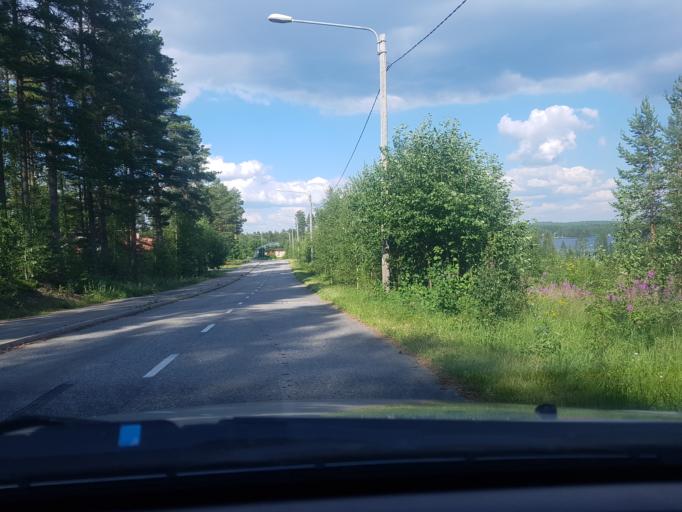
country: FI
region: Kainuu
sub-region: Kehys-Kainuu
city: Kuhmo
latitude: 64.1277
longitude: 29.5414
